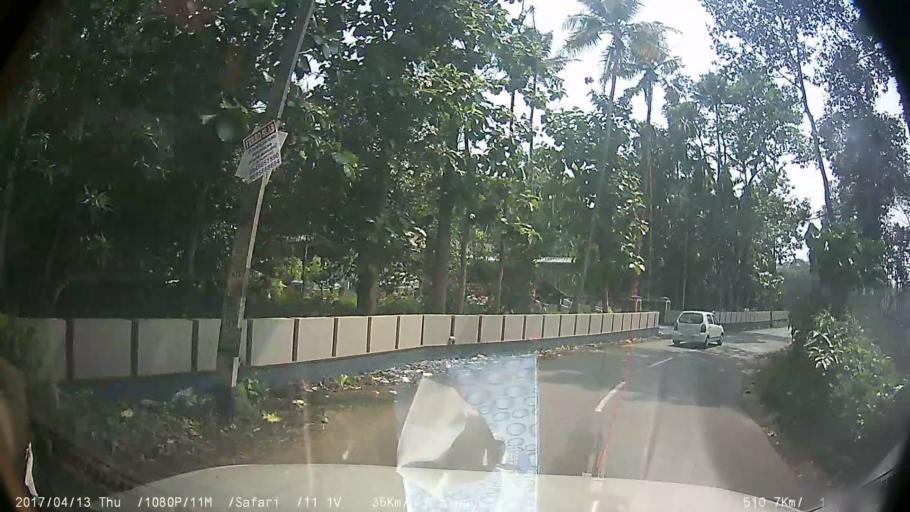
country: IN
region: Kerala
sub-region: Ernakulam
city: Muvattupula
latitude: 10.0287
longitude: 76.5253
